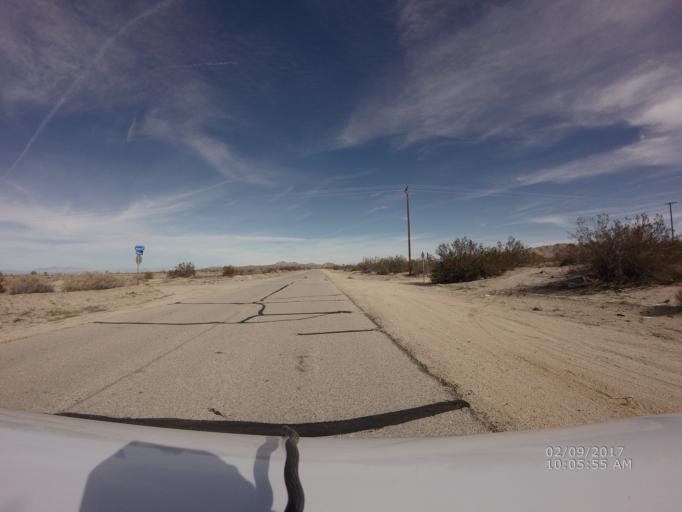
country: US
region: California
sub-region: Los Angeles County
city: Lake Los Angeles
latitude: 34.5724
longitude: -117.8896
